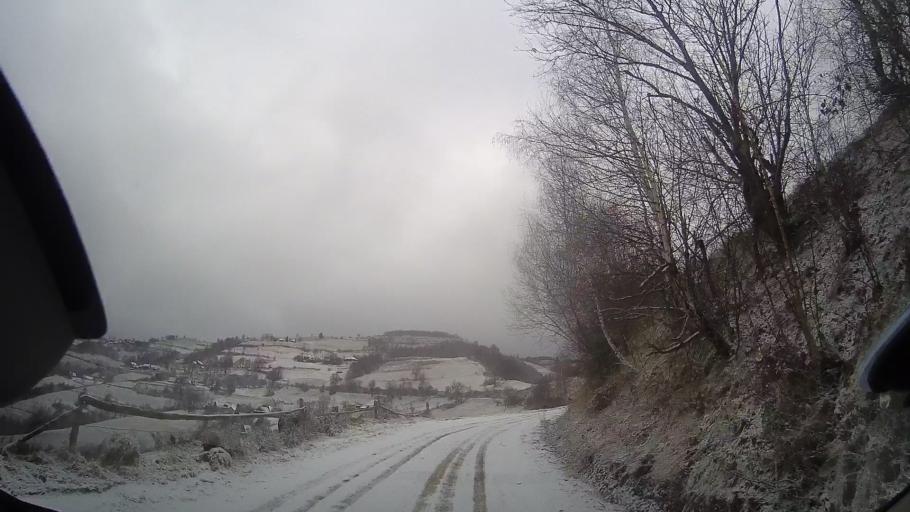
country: RO
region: Cluj
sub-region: Comuna Maguri-Racatau
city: Maguri-Racatau
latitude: 46.6588
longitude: 23.1923
